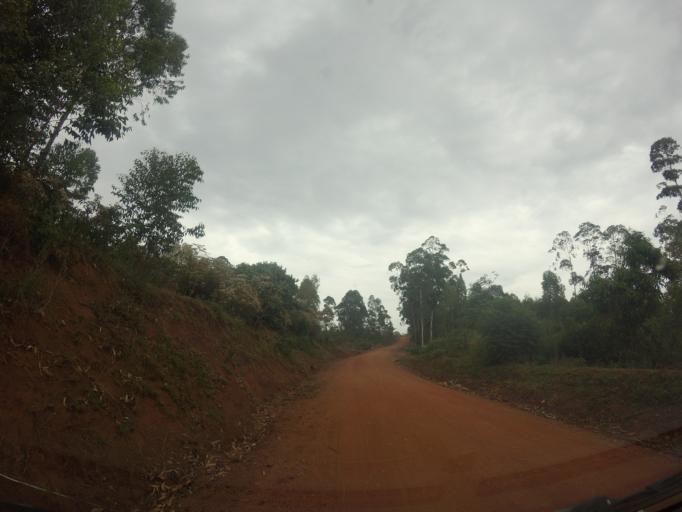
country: UG
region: Northern Region
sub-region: Arua District
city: Arua
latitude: 2.7681
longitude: 30.8587
